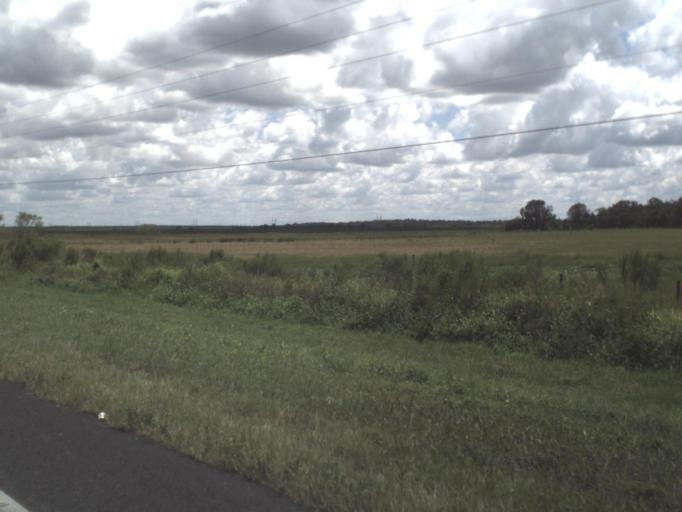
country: US
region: Florida
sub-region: Polk County
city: Alturas
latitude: 27.9141
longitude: -81.7033
